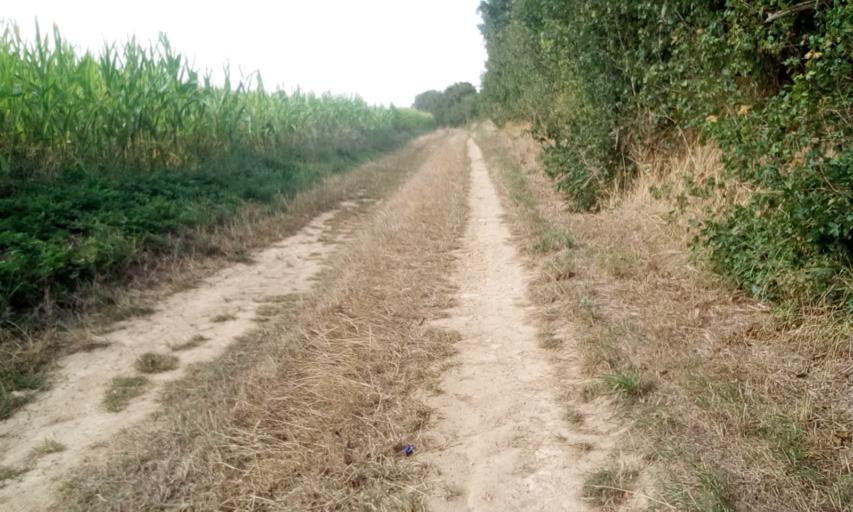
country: FR
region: Lower Normandy
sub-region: Departement du Calvados
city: Saint-Sylvain
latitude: 49.0712
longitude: -0.2297
